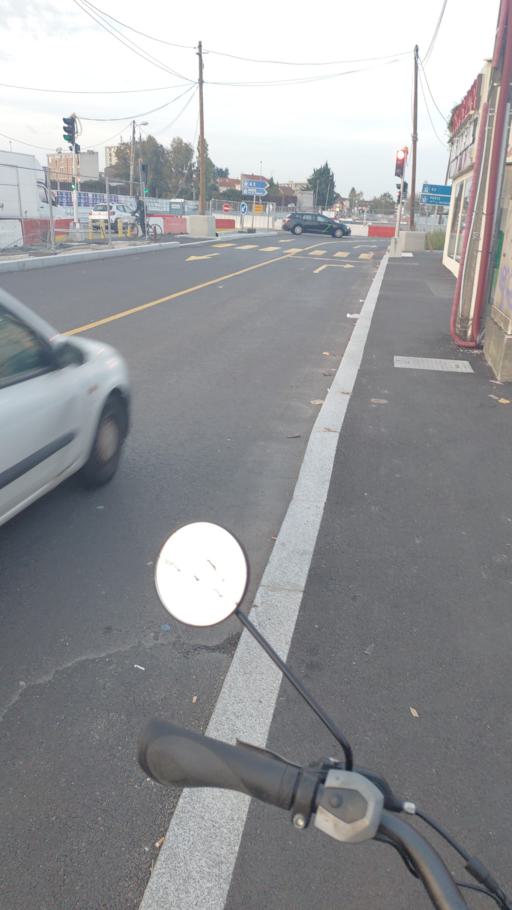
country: FR
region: Ile-de-France
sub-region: Departement de Seine-Saint-Denis
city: Montreuil
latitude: 48.8744
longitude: 2.4407
